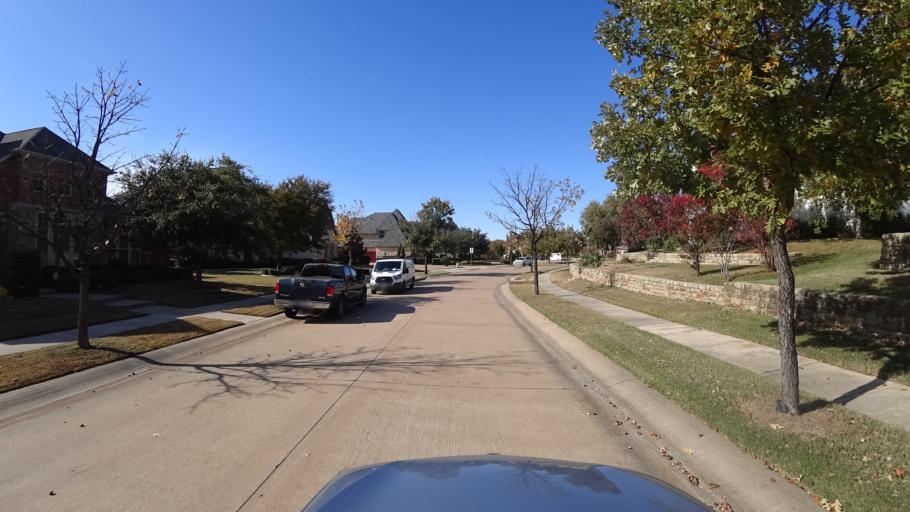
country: US
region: Texas
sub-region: Denton County
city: The Colony
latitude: 33.0299
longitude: -96.9035
